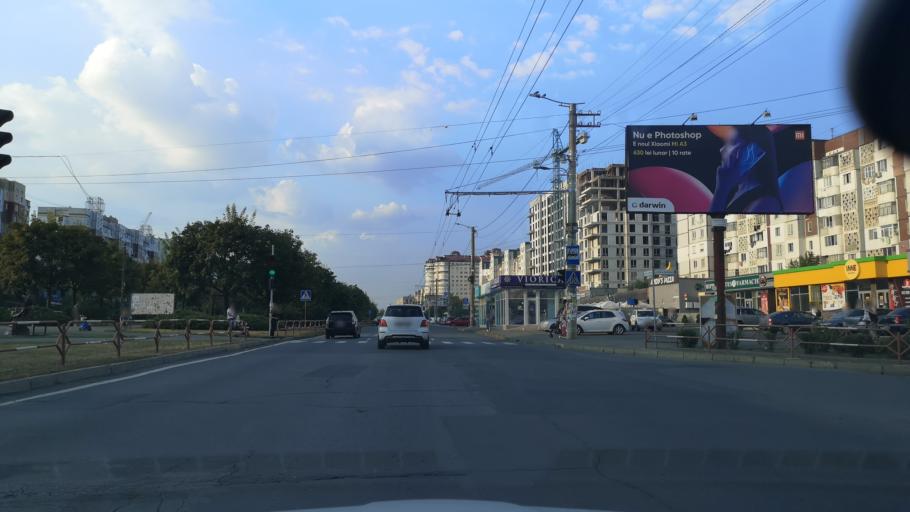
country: MD
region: Chisinau
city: Chisinau
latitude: 47.0433
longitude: 28.8905
